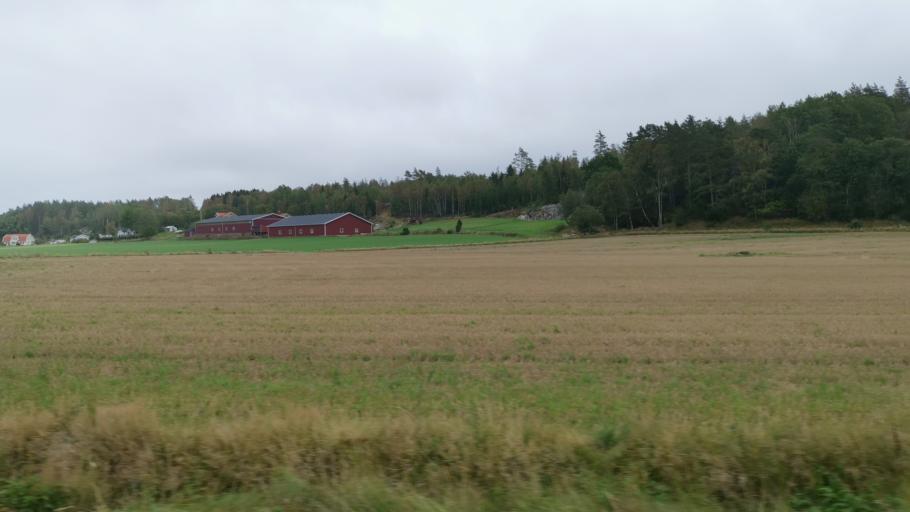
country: SE
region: Vaestra Goetaland
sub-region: Tanums Kommun
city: Tanumshede
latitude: 58.6187
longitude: 11.3578
